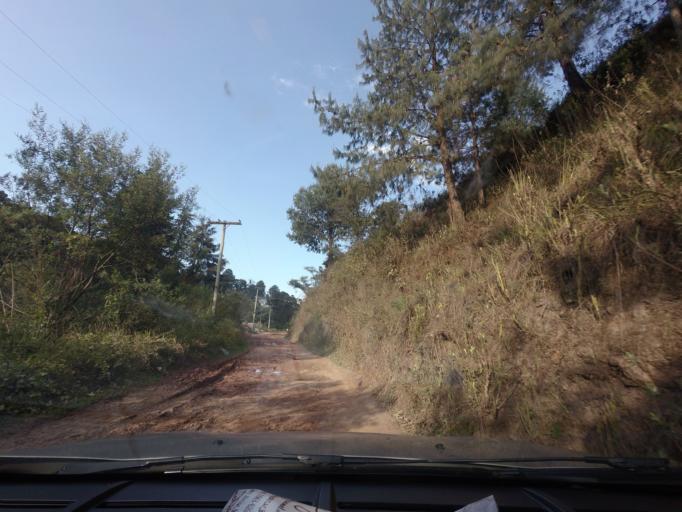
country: BR
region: Sao Paulo
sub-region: Campos Do Jordao
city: Campos do Jordao
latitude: -22.7171
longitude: -45.5544
